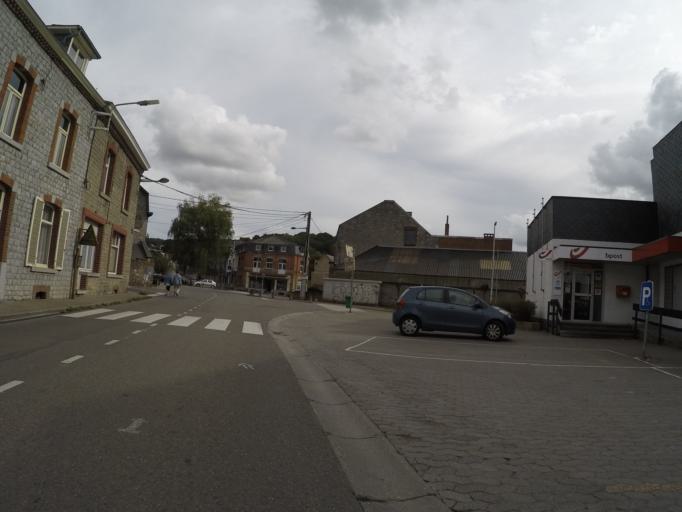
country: BE
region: Wallonia
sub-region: Province de Namur
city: Yvoir
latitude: 50.3281
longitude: 4.8763
